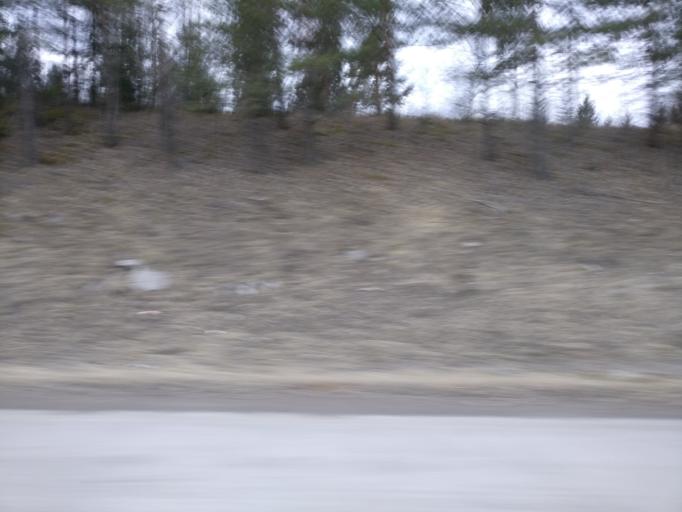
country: FI
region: Uusimaa
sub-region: Helsinki
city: Hyvinge
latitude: 60.6441
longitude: 24.8072
